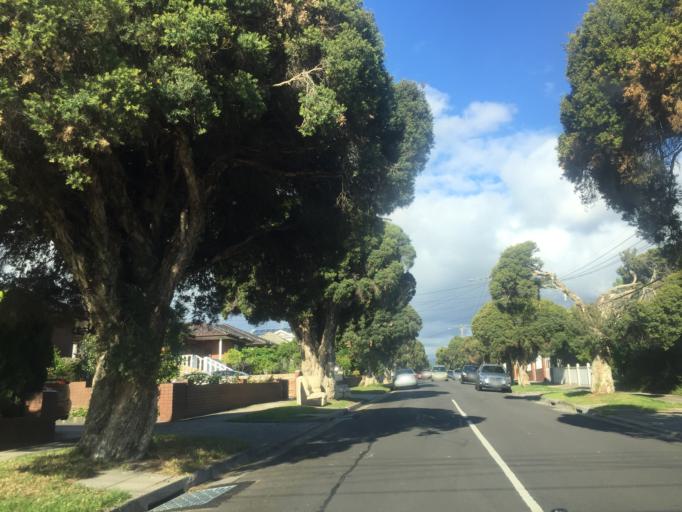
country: AU
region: Victoria
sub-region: Darebin
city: Reservoir
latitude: -37.7330
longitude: 145.0089
